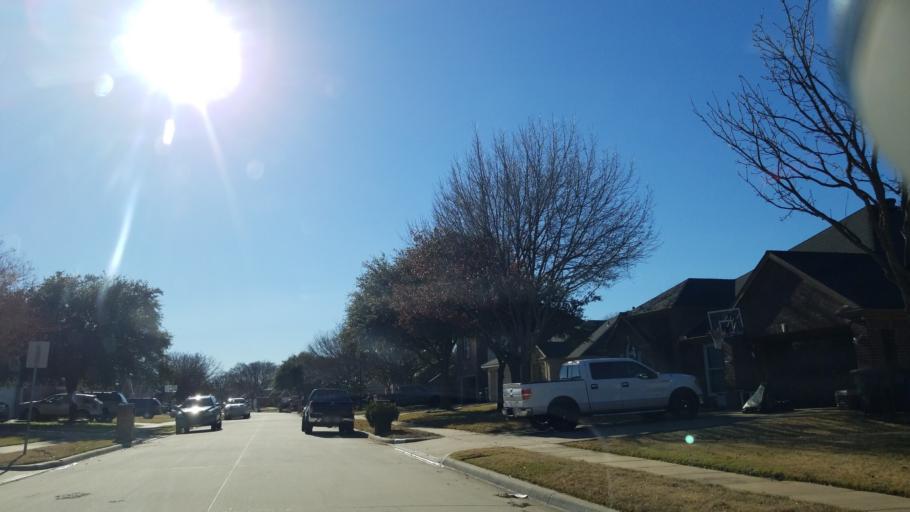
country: US
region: Texas
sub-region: Denton County
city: Corinth
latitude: 33.1406
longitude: -97.0853
